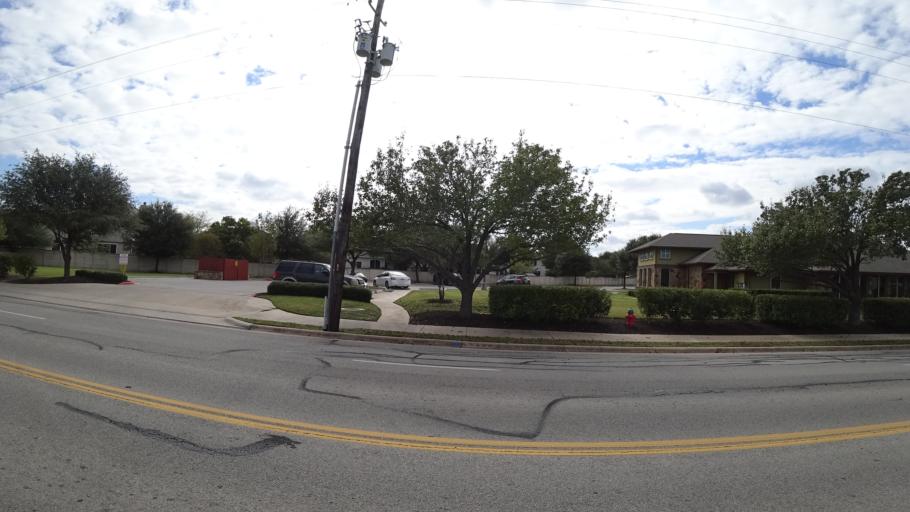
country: US
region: Texas
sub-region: Travis County
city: Windemere
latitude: 30.4425
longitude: -97.6426
